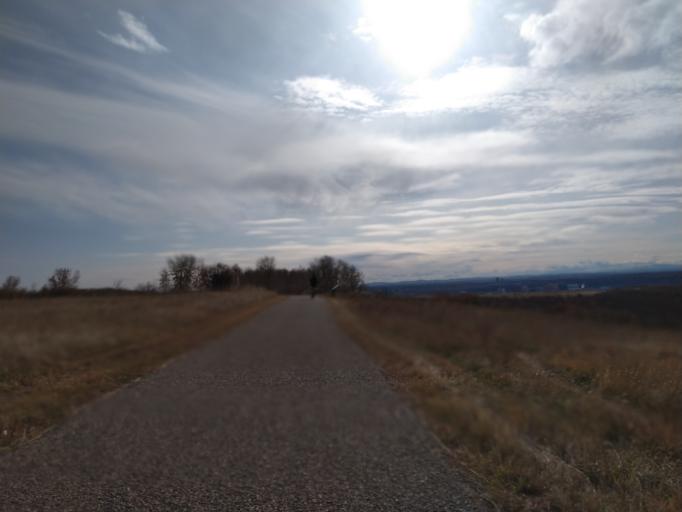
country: CA
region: Alberta
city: Calgary
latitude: 51.1058
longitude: -114.1138
